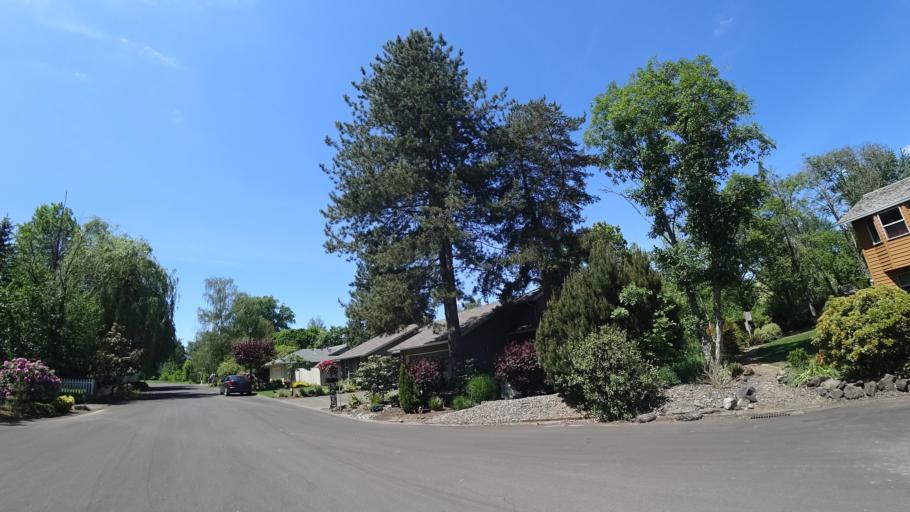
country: US
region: Oregon
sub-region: Washington County
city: King City
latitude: 45.4317
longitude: -122.8022
